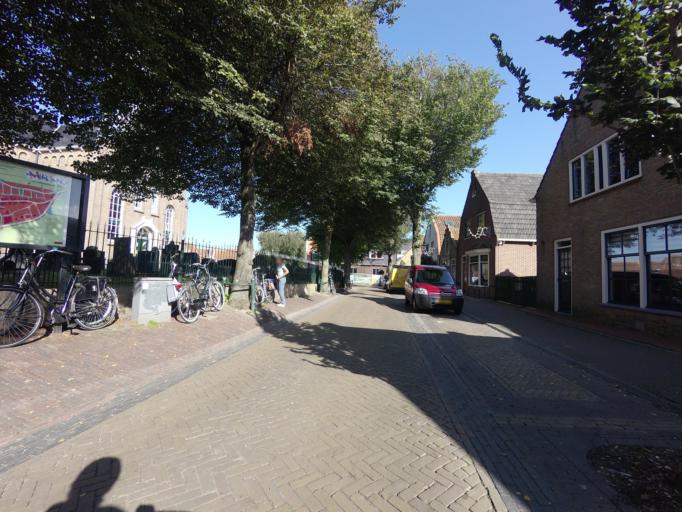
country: NL
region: Friesland
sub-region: Gemeente Terschelling
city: West-Terschelling
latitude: 53.3827
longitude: 5.2848
